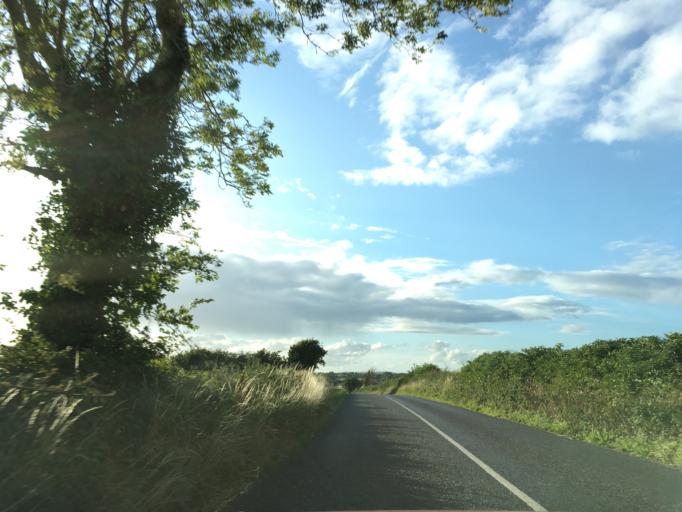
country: IE
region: Munster
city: Cashel
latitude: 52.4762
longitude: -7.9263
